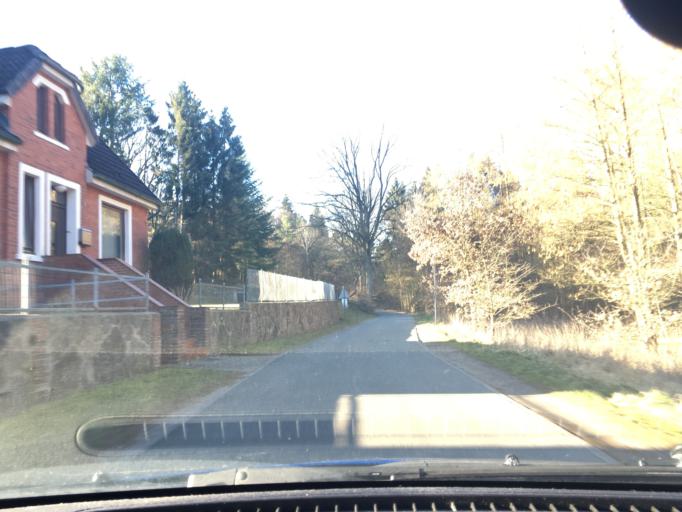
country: DE
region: Schleswig-Holstein
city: Schnakenbek
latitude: 53.3796
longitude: 10.5075
